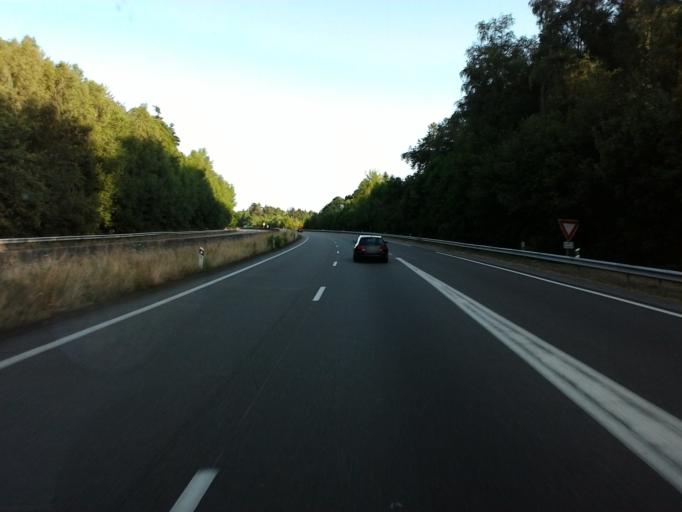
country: FR
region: Lorraine
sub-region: Departement des Vosges
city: Epinal
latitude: 48.1730
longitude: 6.4827
